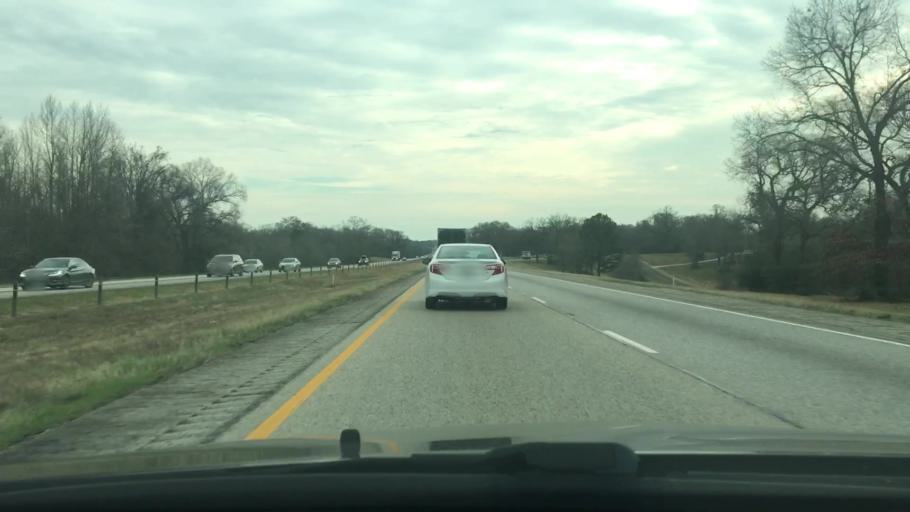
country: US
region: Texas
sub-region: Leon County
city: Centerville
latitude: 31.1992
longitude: -95.9944
